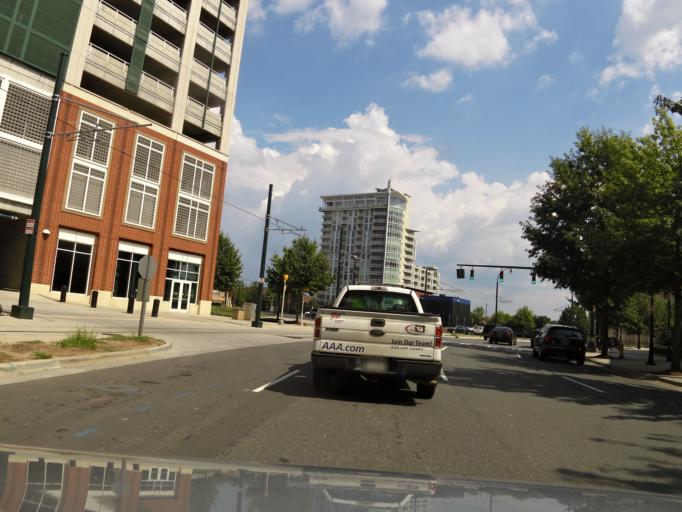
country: US
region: North Carolina
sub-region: Mecklenburg County
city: Charlotte
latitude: 35.2261
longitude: -80.8387
